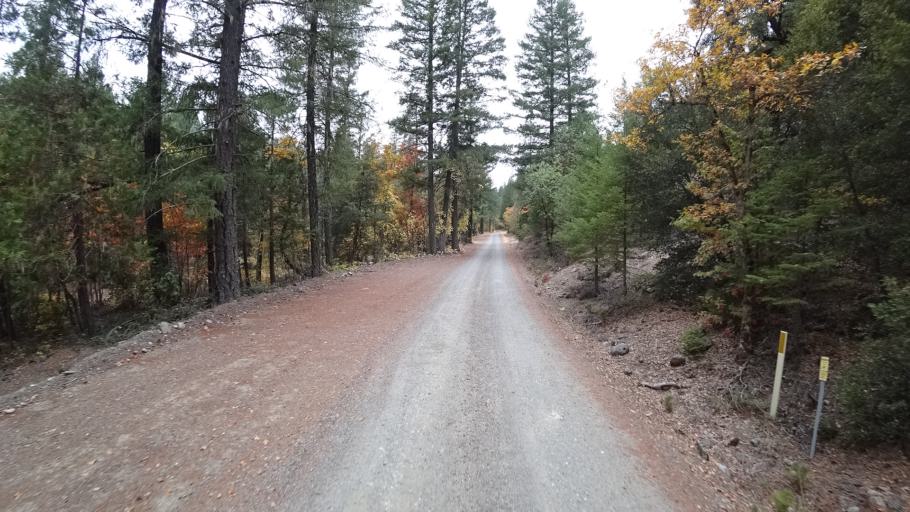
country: US
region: California
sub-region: Siskiyou County
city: Happy Camp
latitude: 41.8782
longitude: -123.4411
